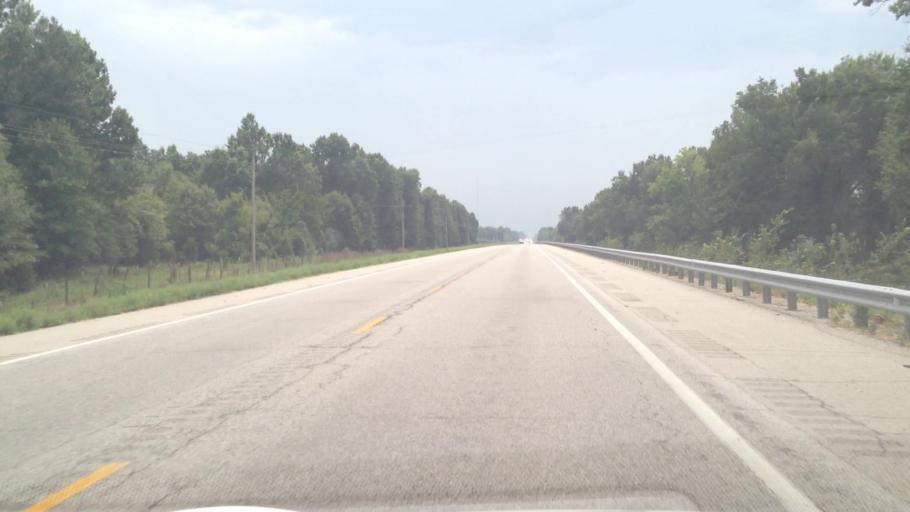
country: US
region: Kansas
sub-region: Cherokee County
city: Galena
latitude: 37.1409
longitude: -94.7044
